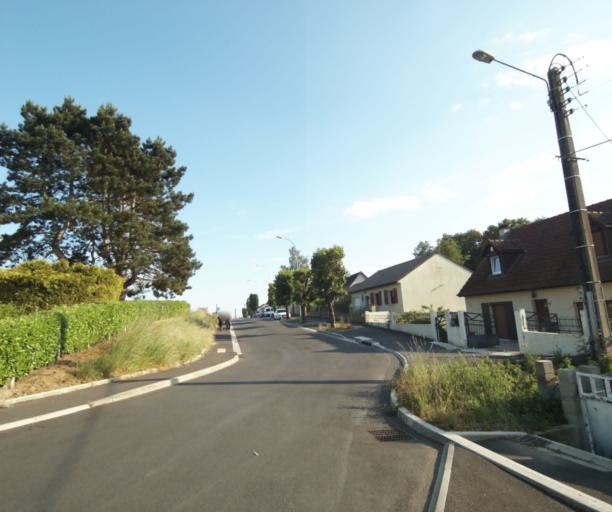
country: FR
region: Champagne-Ardenne
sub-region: Departement des Ardennes
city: Charleville-Mezieres
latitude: 49.7898
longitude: 4.7097
